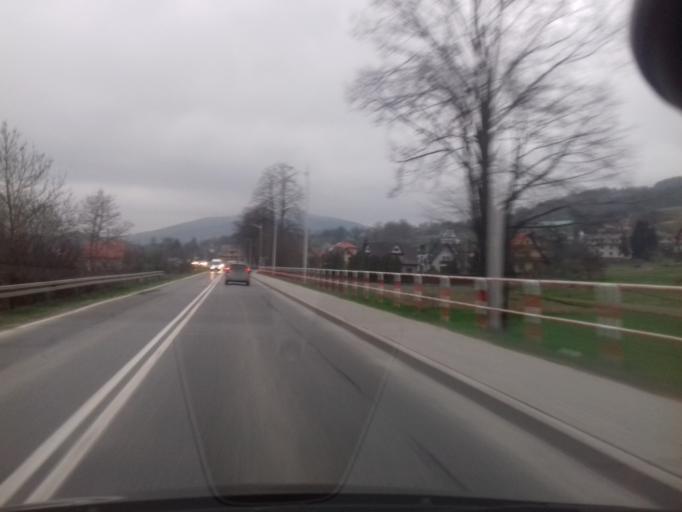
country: PL
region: Lesser Poland Voivodeship
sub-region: Powiat limanowski
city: Mszana Dolna
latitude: 49.6871
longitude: 20.0496
